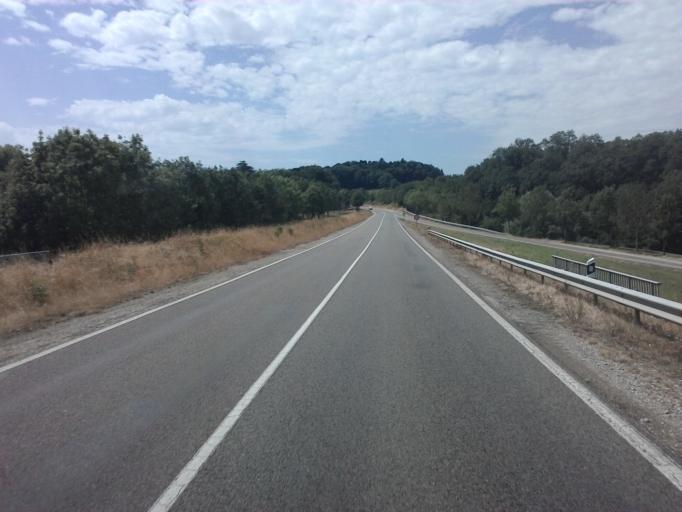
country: FR
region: Bourgogne
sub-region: Departement de Saone-et-Loire
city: Cuiseaux
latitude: 46.4818
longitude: 5.3667
